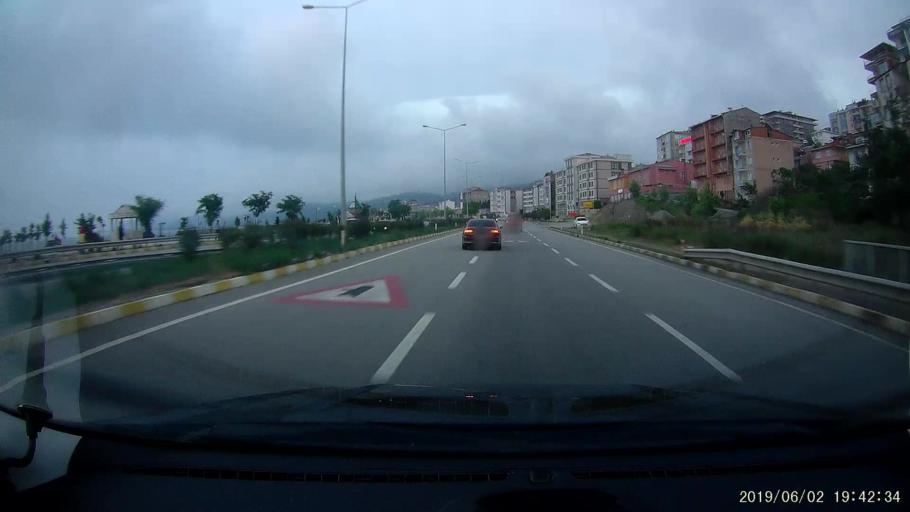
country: TR
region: Giresun
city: Kesap
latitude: 40.9175
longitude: 38.5079
